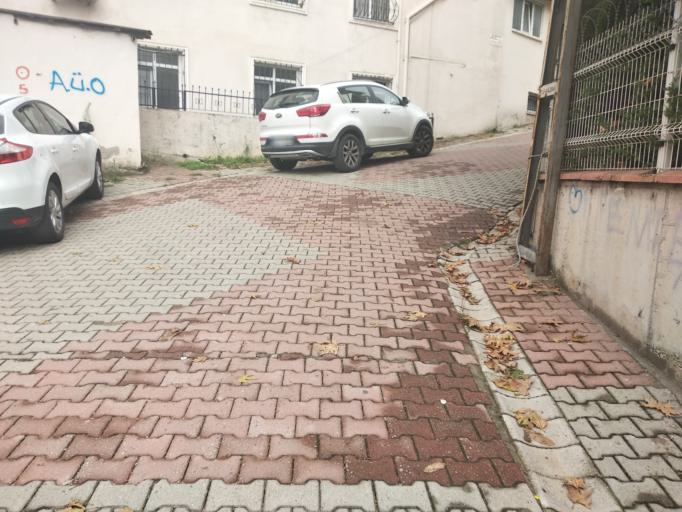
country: TR
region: Istanbul
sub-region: Atasehir
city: Atasehir
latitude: 40.9831
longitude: 29.1155
